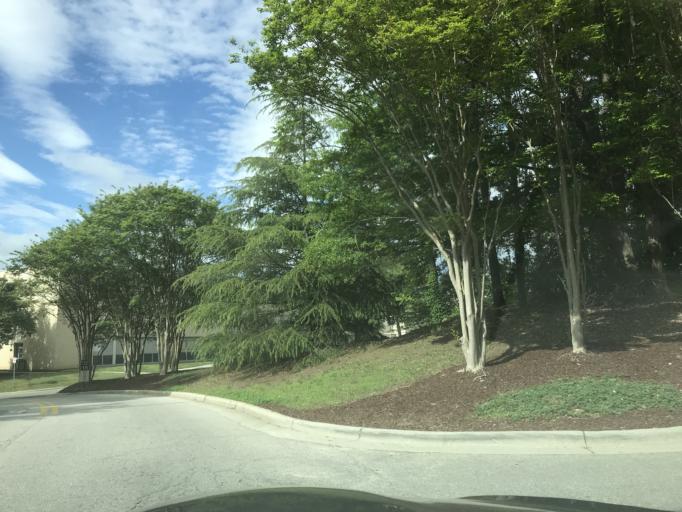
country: US
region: North Carolina
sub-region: Wake County
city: Raleigh
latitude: 35.7836
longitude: -78.5862
